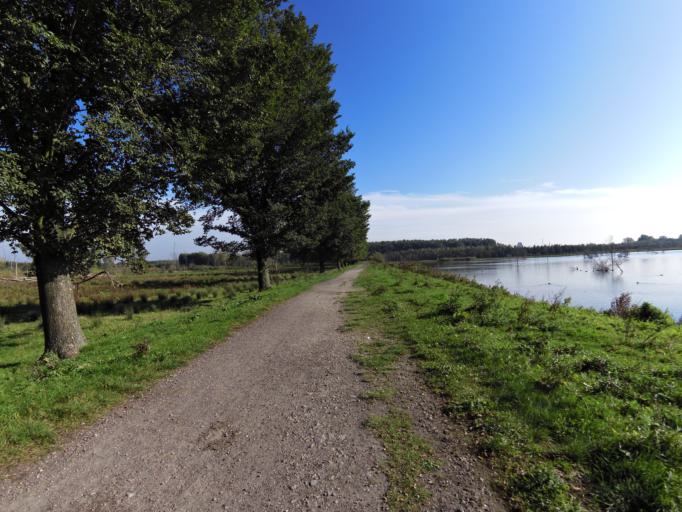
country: NL
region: South Holland
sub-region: Gemeente Vlaardingen
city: Vlaardingen
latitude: 51.9269
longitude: 4.3225
